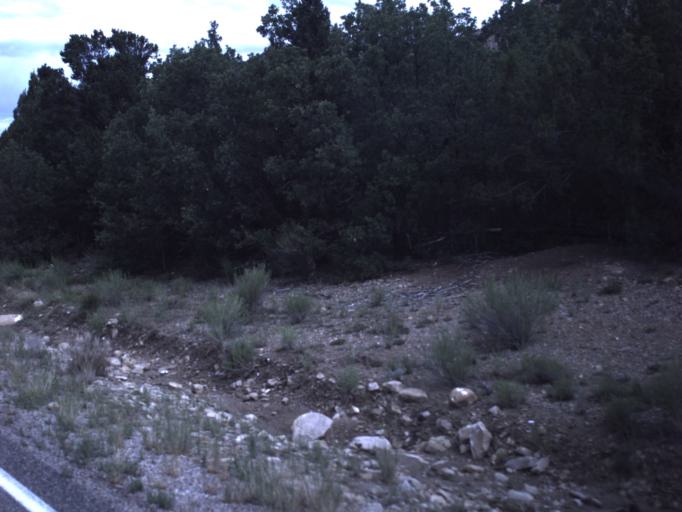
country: US
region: Utah
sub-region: Iron County
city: Cedar City
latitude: 37.6542
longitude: -112.9884
